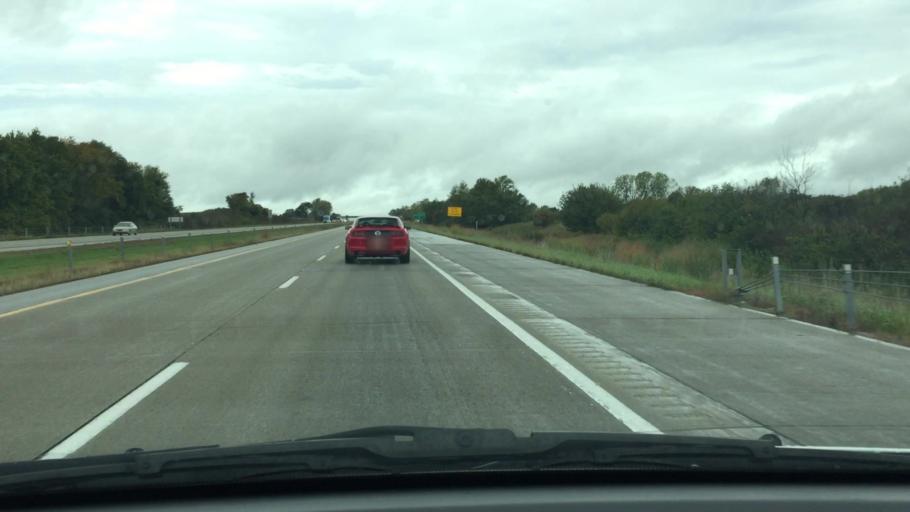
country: US
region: Iowa
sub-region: Polk County
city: Mitchellville
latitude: 41.6808
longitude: -93.3550
